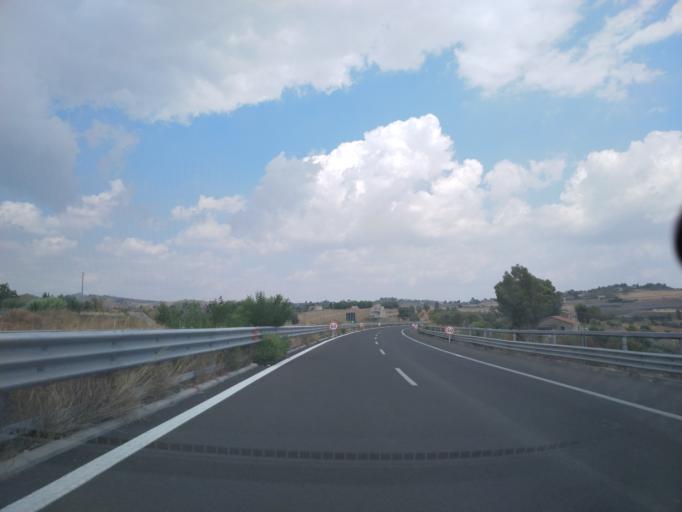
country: IT
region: Sicily
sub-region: Agrigento
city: Racalmuto
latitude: 37.3904
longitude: 13.7483
